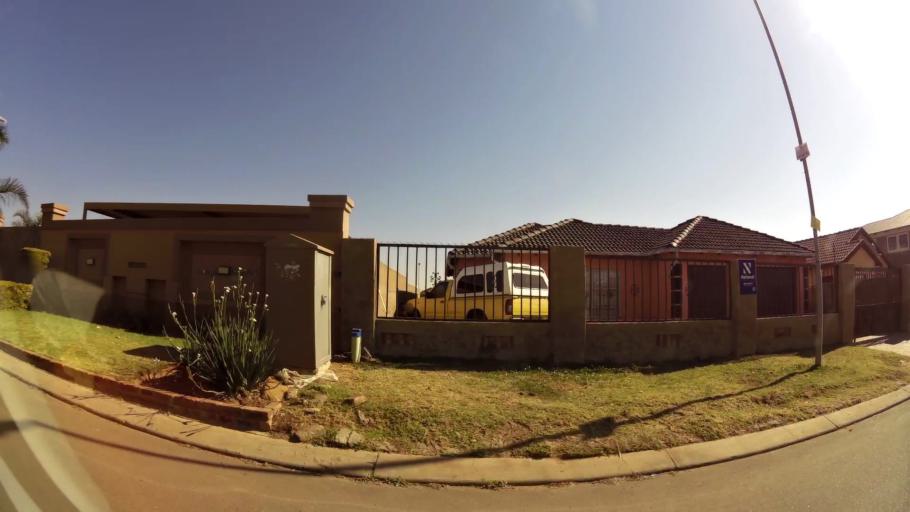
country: ZA
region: Gauteng
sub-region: Ekurhuleni Metropolitan Municipality
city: Tembisa
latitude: -26.0396
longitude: 28.2031
